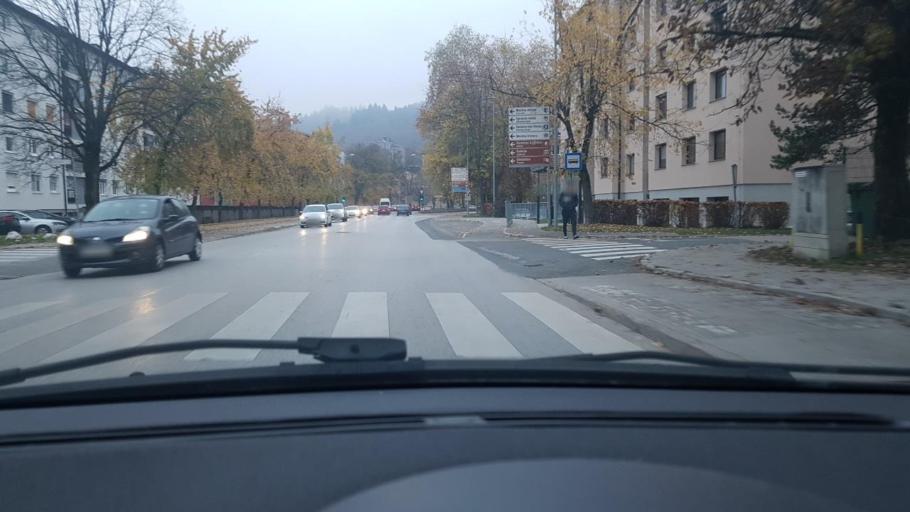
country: SI
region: Celje
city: Celje
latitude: 46.2359
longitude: 15.2537
